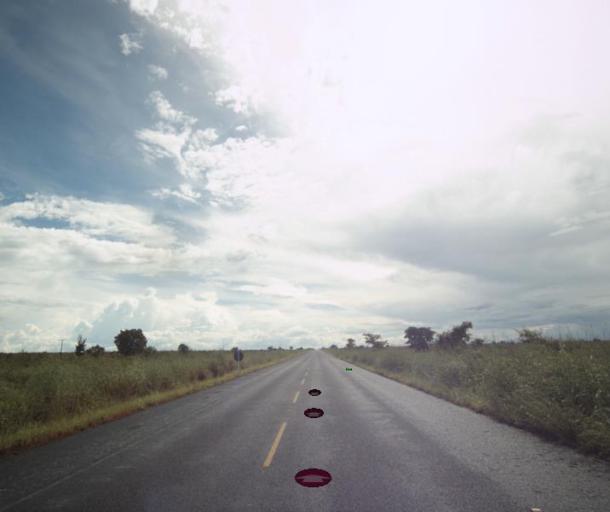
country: BR
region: Goias
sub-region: Sao Miguel Do Araguaia
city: Sao Miguel do Araguaia
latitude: -13.2958
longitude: -50.3585
